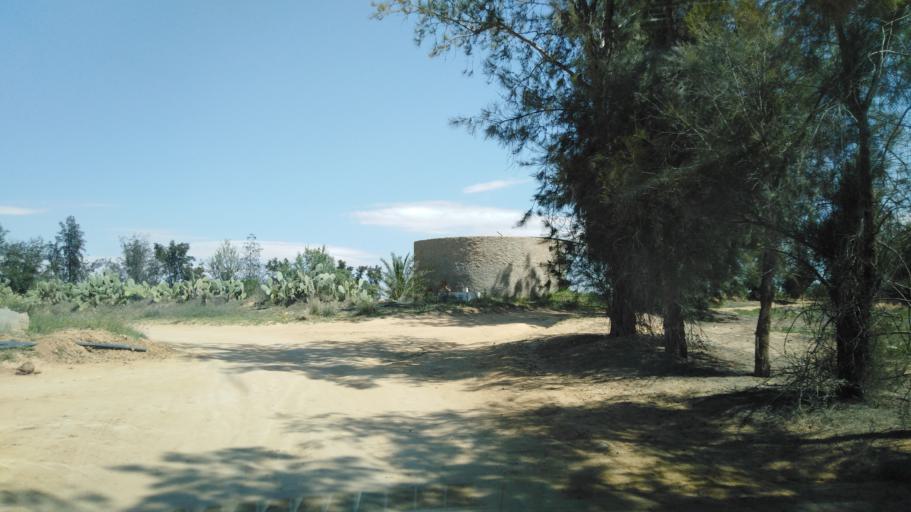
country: TN
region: Safaqis
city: Sfax
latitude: 34.7714
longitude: 10.5279
